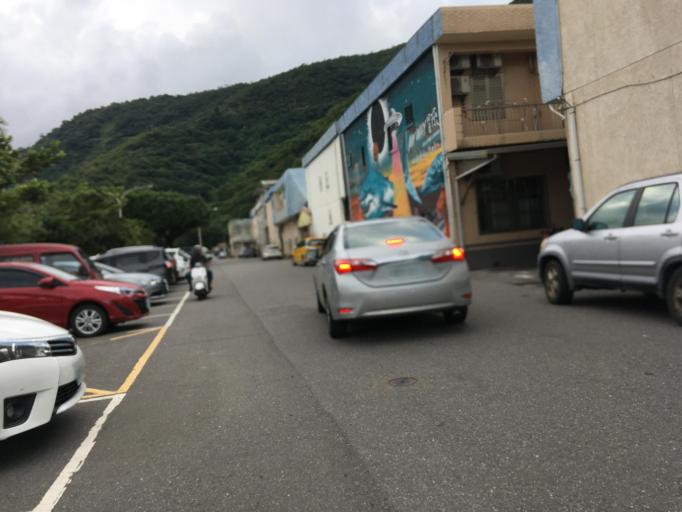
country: TW
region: Taiwan
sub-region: Yilan
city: Yilan
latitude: 24.5772
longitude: 121.8697
